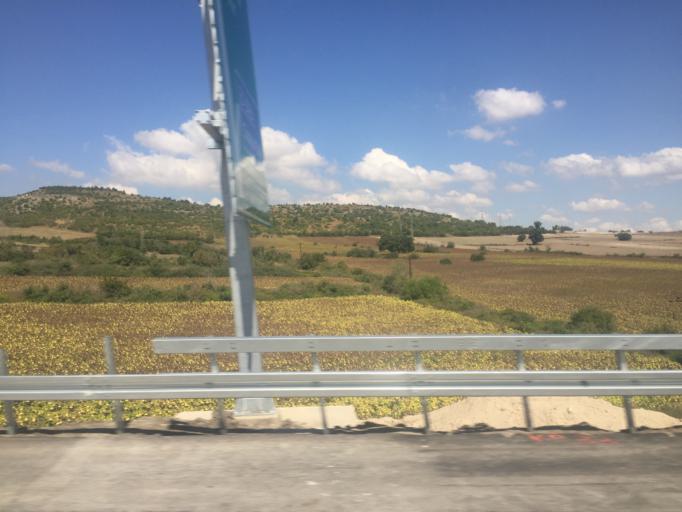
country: TR
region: Balikesir
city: Gobel
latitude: 39.9771
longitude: 28.1706
